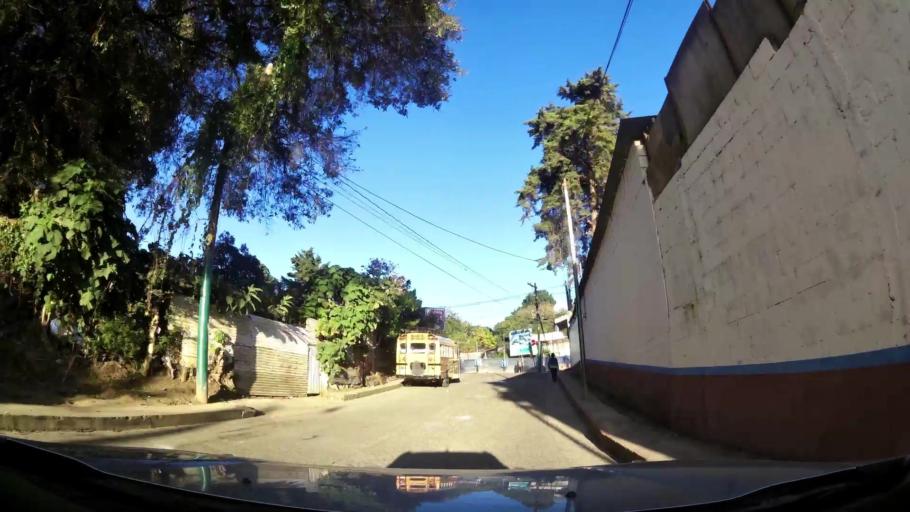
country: GT
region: Sacatepequez
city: San Lucas Sacatepequez
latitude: 14.6133
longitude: -90.6555
